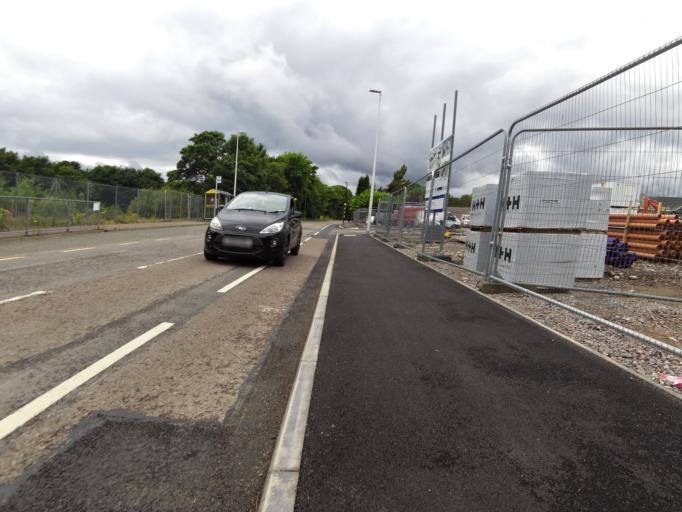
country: GB
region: Scotland
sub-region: Highland
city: Fort William
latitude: 56.8342
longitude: -5.0872
